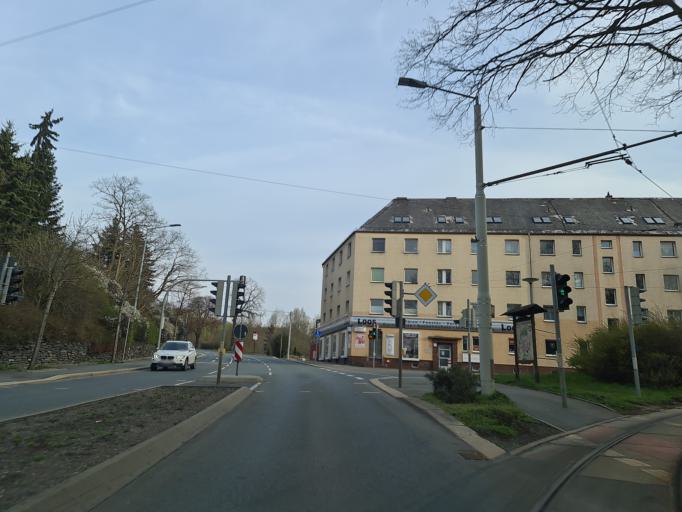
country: DE
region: Saxony
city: Plauen
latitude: 50.4805
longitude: 12.1409
